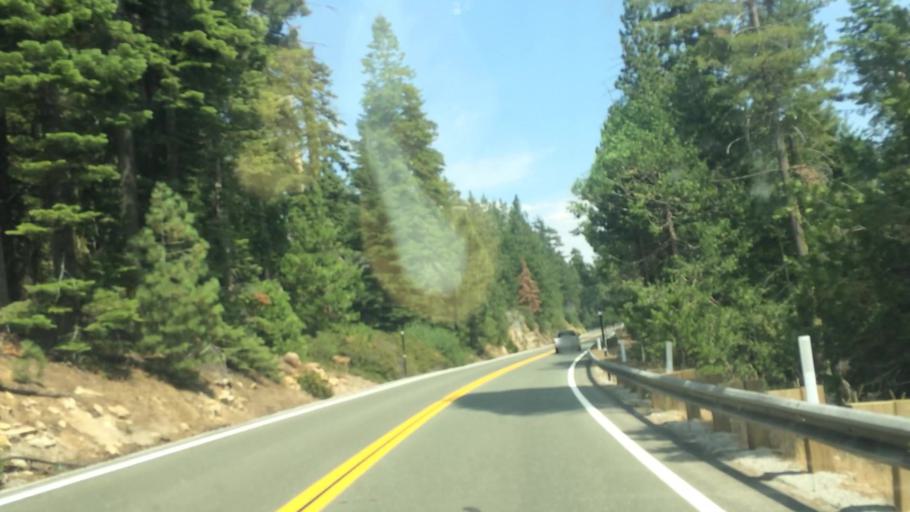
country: US
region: California
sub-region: Amador County
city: Pioneer
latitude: 38.5447
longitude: -120.3311
